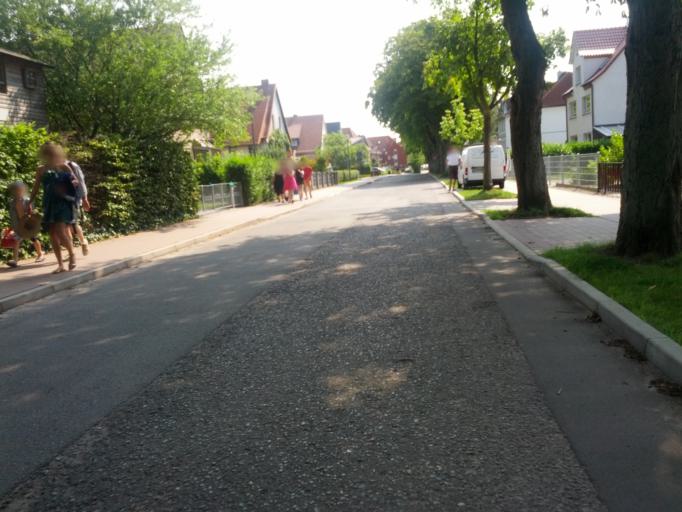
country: DE
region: Mecklenburg-Vorpommern
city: Bastorf
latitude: 54.1087
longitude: 11.6158
